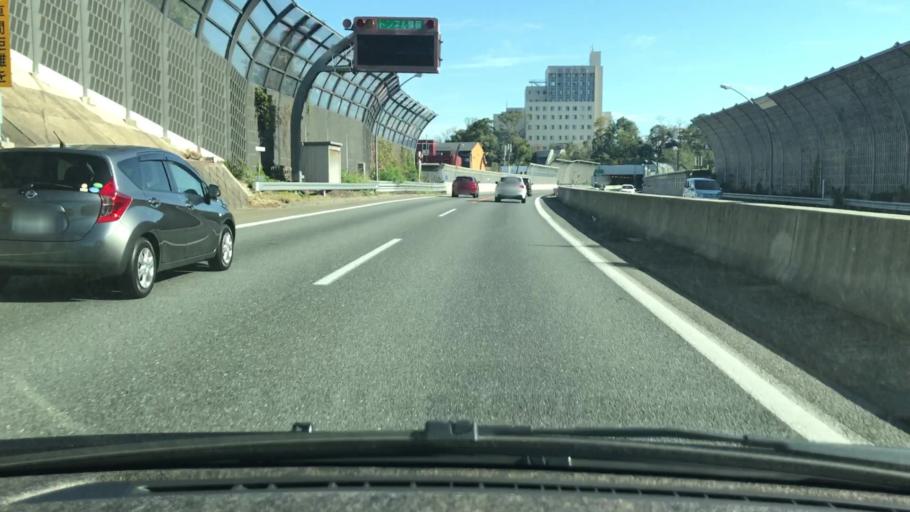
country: JP
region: Osaka
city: Suita
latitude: 34.7714
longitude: 135.5043
